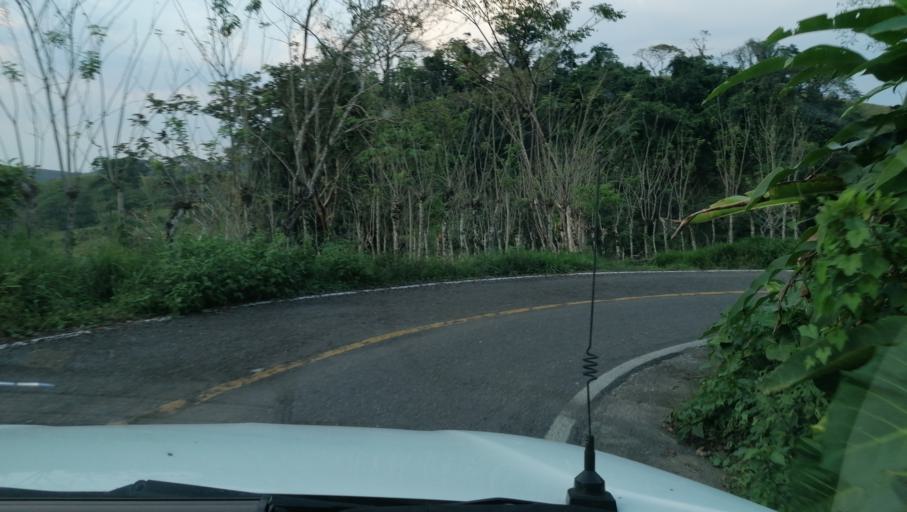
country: MX
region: Chiapas
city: Pichucalco
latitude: 17.5143
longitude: -93.2061
